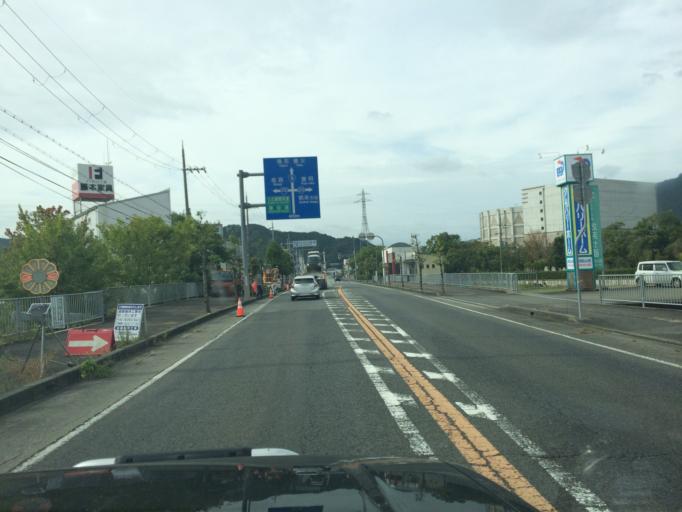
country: JP
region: Hyogo
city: Toyooka
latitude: 35.3306
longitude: 134.8656
